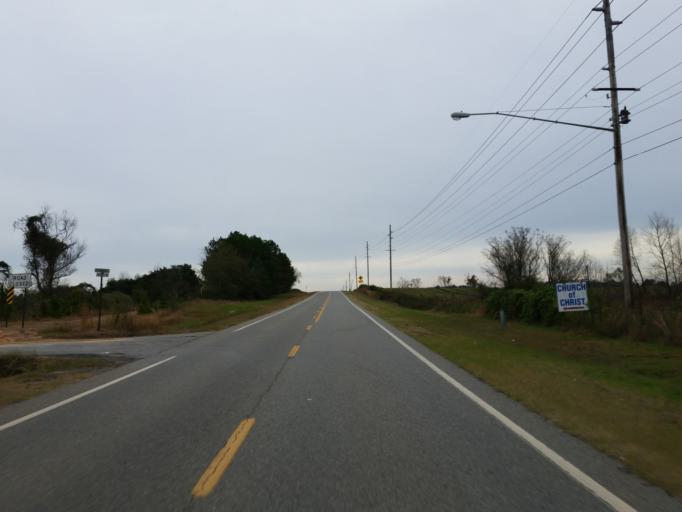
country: US
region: Georgia
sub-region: Crisp County
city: Cordele
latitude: 31.9149
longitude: -83.7101
